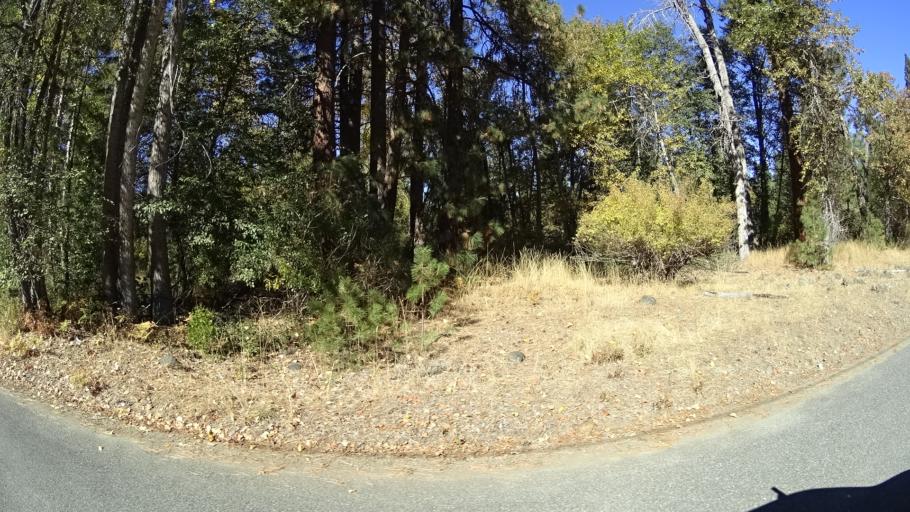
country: US
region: California
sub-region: Siskiyou County
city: Yreka
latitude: 41.5316
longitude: -122.9445
